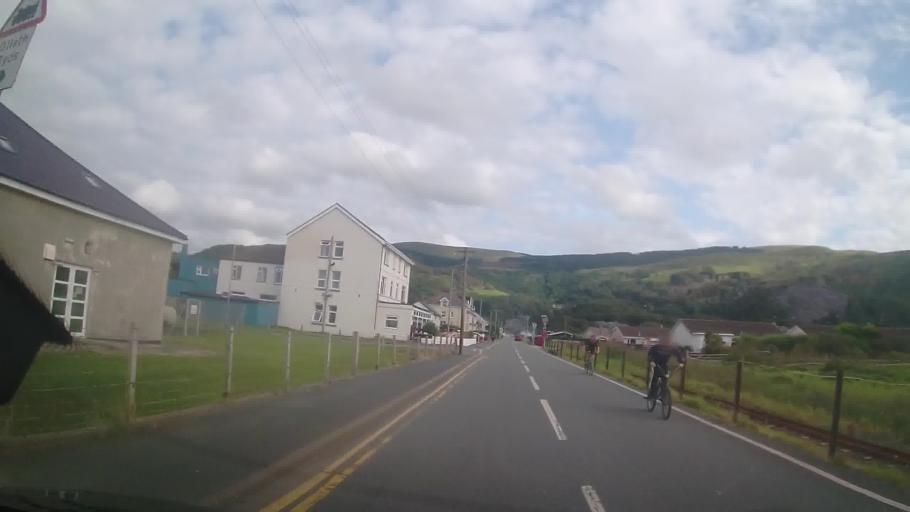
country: GB
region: Wales
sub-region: Gwynedd
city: Barmouth
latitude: 52.6970
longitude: -4.0539
